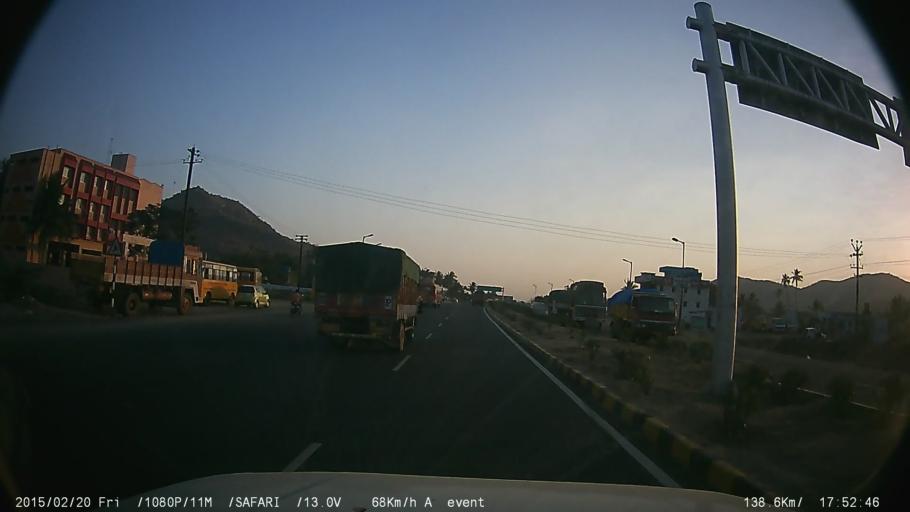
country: IN
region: Tamil Nadu
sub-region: Krishnagiri
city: Krishnagiri
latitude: 12.5003
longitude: 78.2230
